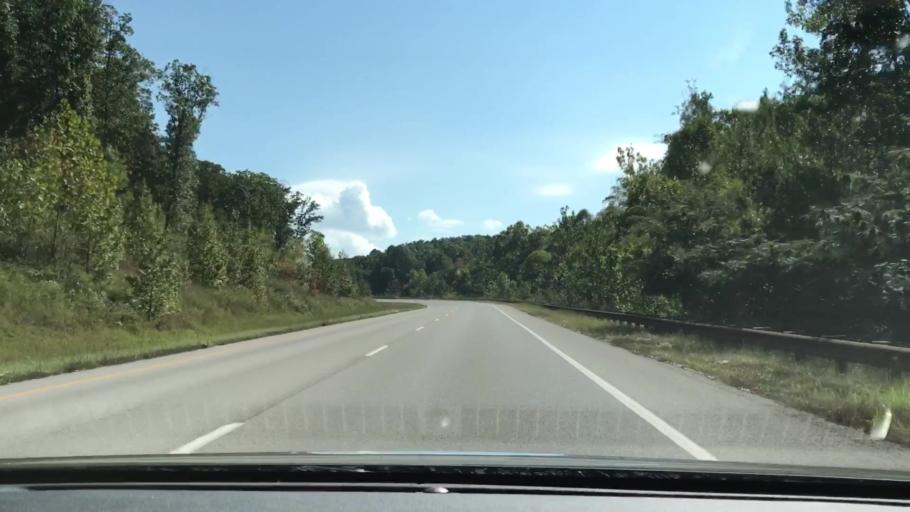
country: US
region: Kentucky
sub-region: Trigg County
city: Cadiz
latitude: 36.7783
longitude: -88.0889
